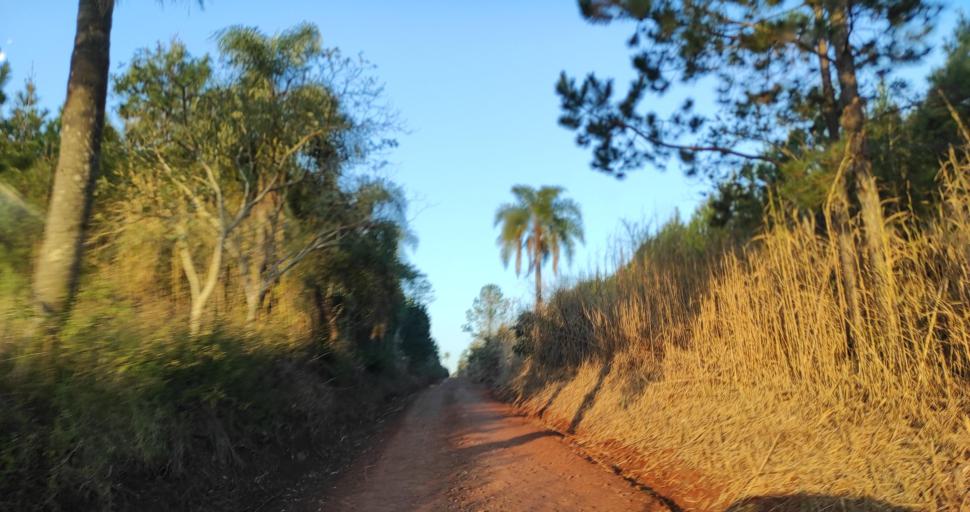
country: AR
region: Misiones
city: Capiovi
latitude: -26.8808
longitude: -55.1128
